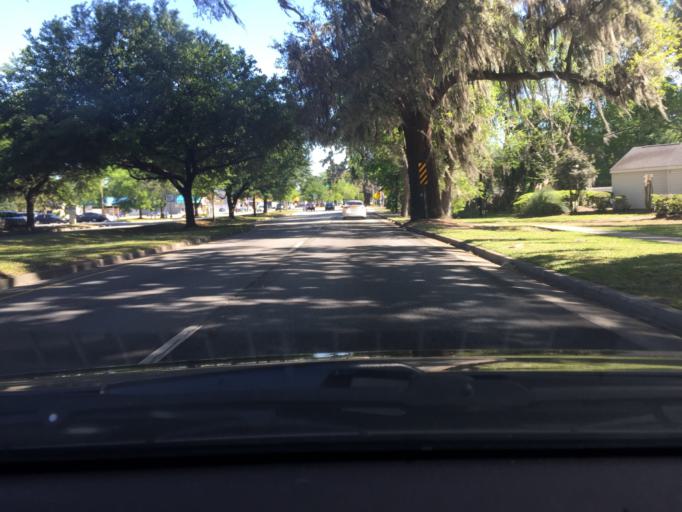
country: US
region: Georgia
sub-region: Chatham County
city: Montgomery
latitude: 31.9897
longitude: -81.1283
